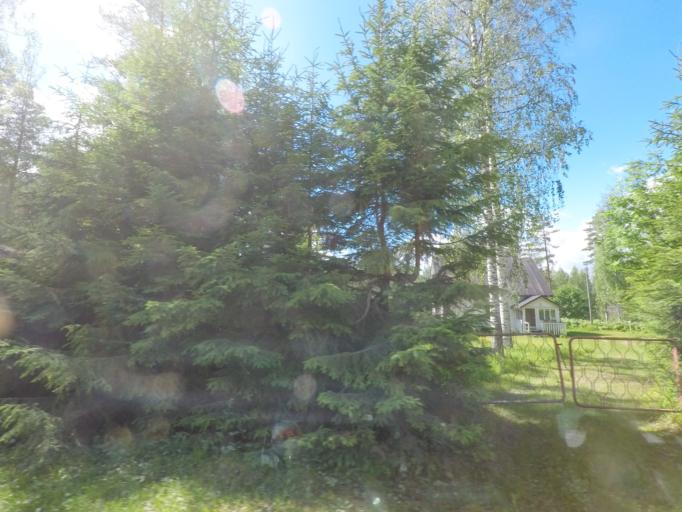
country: FI
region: Central Finland
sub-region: Jyvaeskylae
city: Hankasalmi
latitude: 62.4379
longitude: 26.6448
